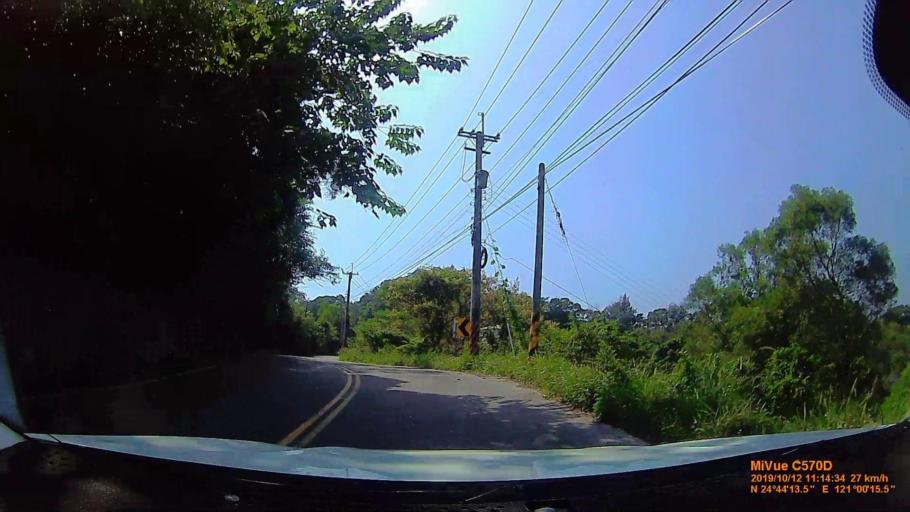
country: TW
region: Taiwan
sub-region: Hsinchu
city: Hsinchu
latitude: 24.7370
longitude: 121.0043
